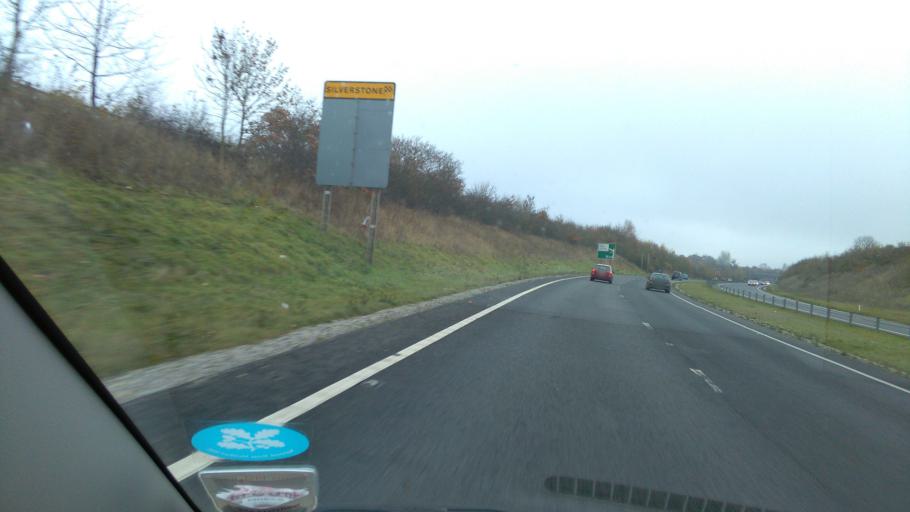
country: GB
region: England
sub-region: Northamptonshire
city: Silverstone
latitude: 52.0911
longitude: -1.0157
